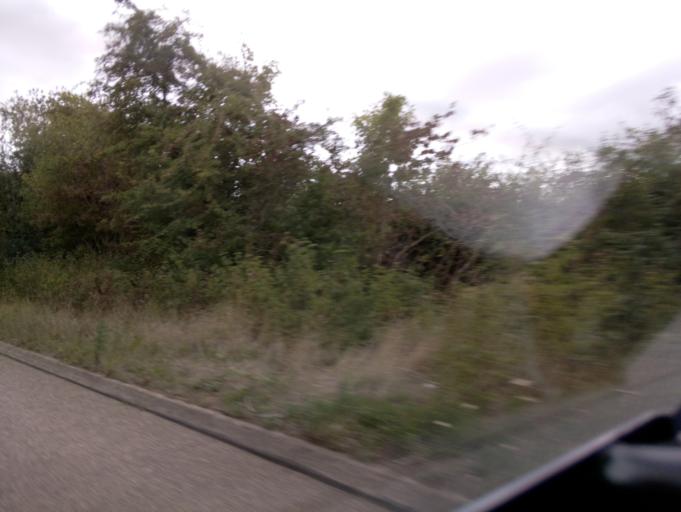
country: GB
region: England
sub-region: Devon
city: Exminster
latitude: 50.6830
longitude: -3.4907
